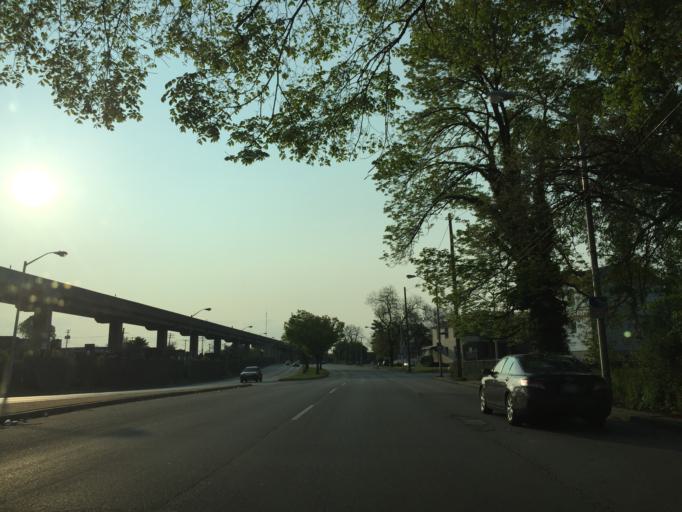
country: US
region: Maryland
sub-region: Baltimore County
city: Lochearn
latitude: 39.3424
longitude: -76.6878
